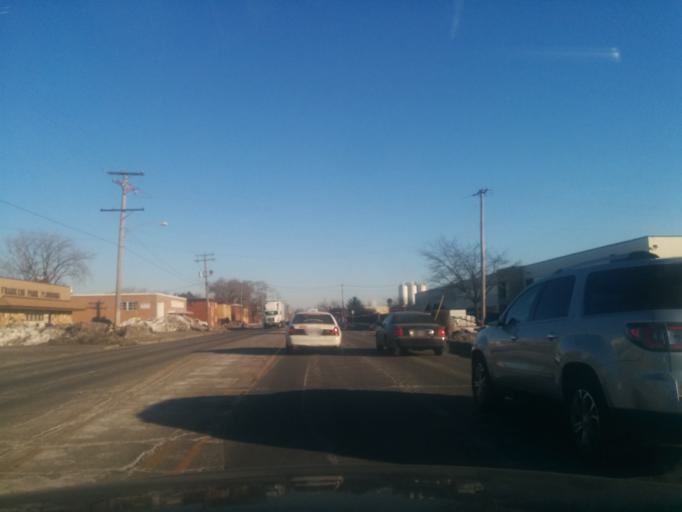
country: US
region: Illinois
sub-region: Cook County
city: Franklin Park
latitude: 41.9231
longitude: -87.8649
